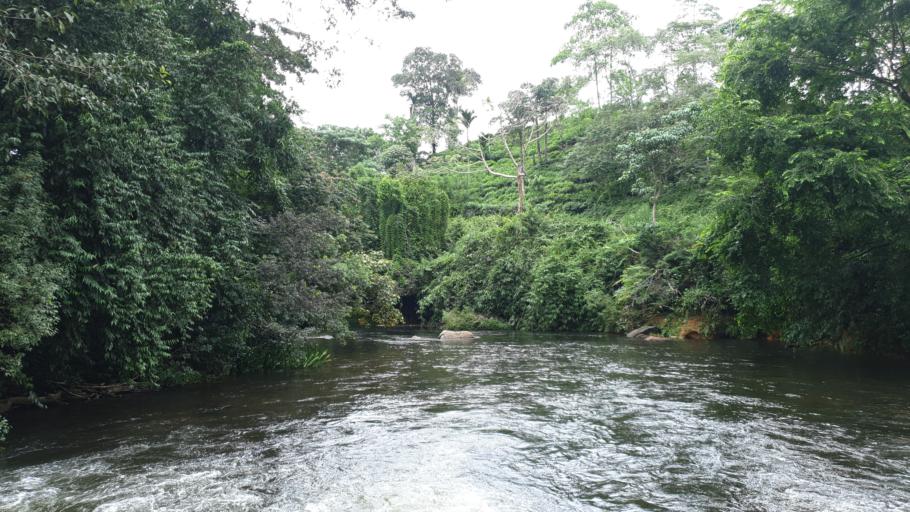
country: LK
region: Sabaragamuwa
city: Ratnapura
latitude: 6.4234
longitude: 80.5303
